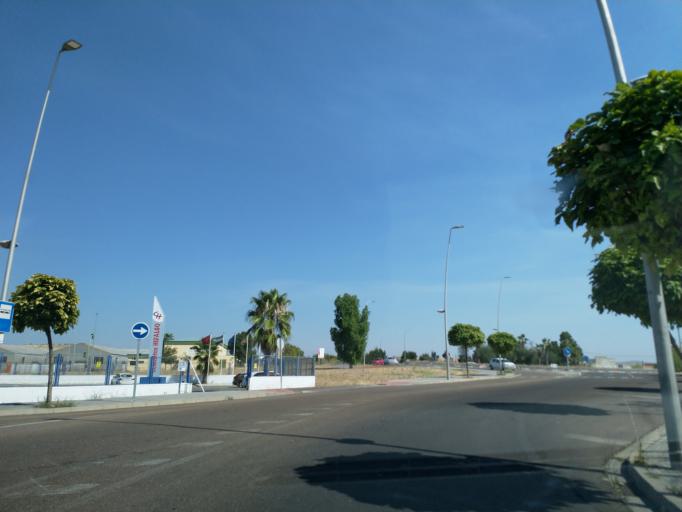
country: ES
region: Extremadura
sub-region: Provincia de Badajoz
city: Merida
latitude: 38.9351
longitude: -6.3458
